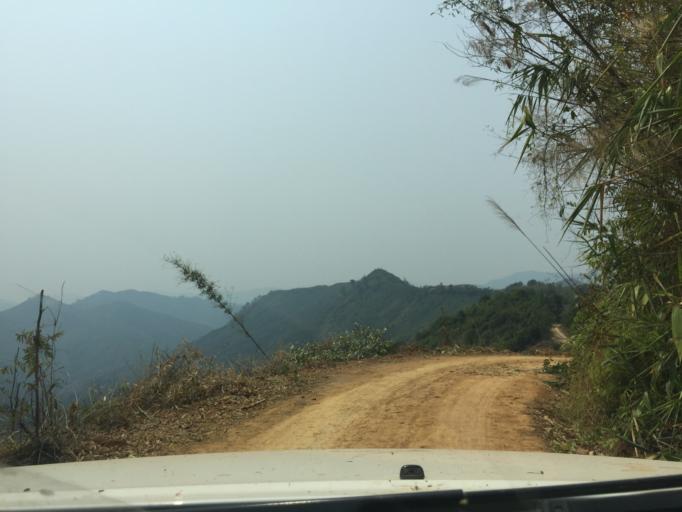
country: LA
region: Loungnamtha
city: Muang Nale
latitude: 20.6293
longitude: 101.6327
